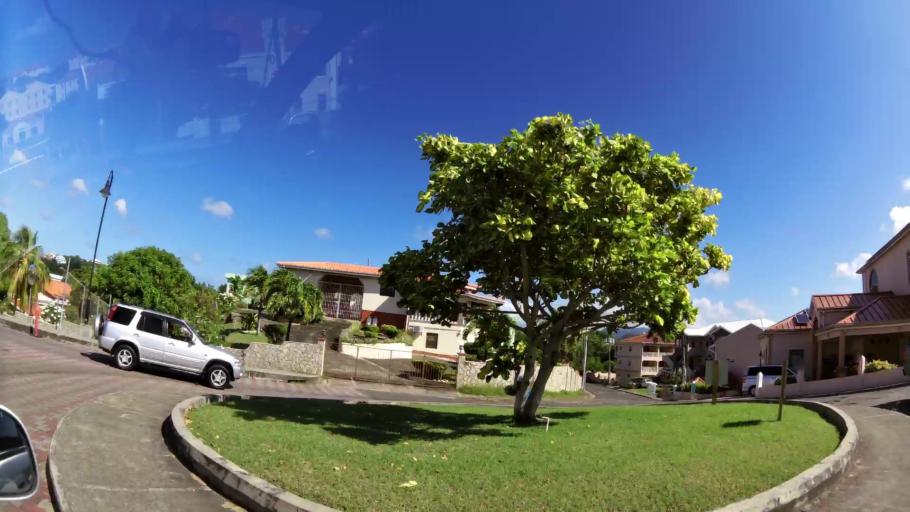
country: GD
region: Saint George
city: Saint George's
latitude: 12.0015
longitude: -61.7721
